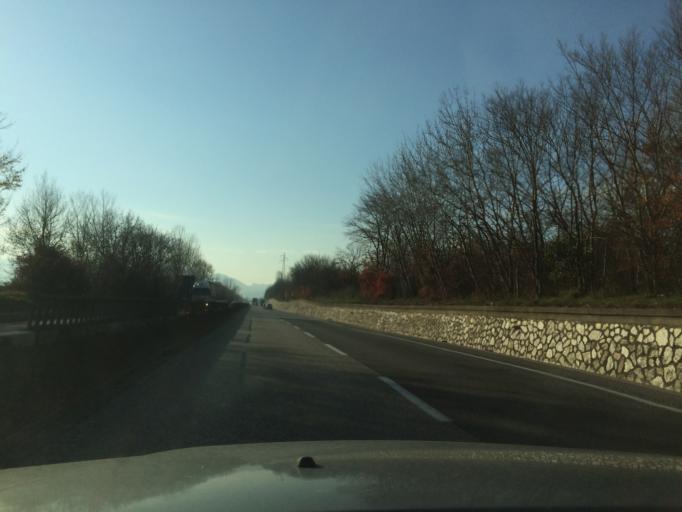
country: IT
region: Umbria
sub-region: Provincia di Terni
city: San Gemini
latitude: 42.5663
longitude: 12.5584
